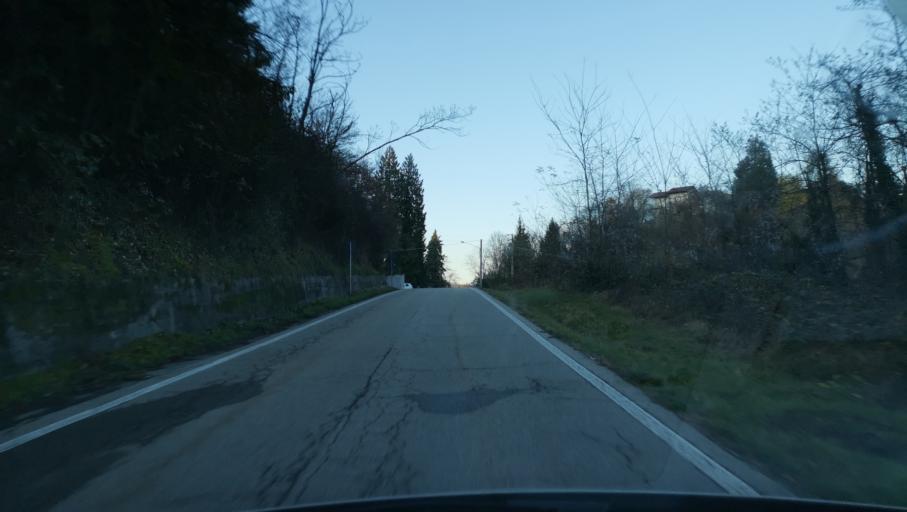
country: IT
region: Piedmont
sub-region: Provincia di Asti
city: Berzano di San Pietro
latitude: 45.0904
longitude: 7.9510
